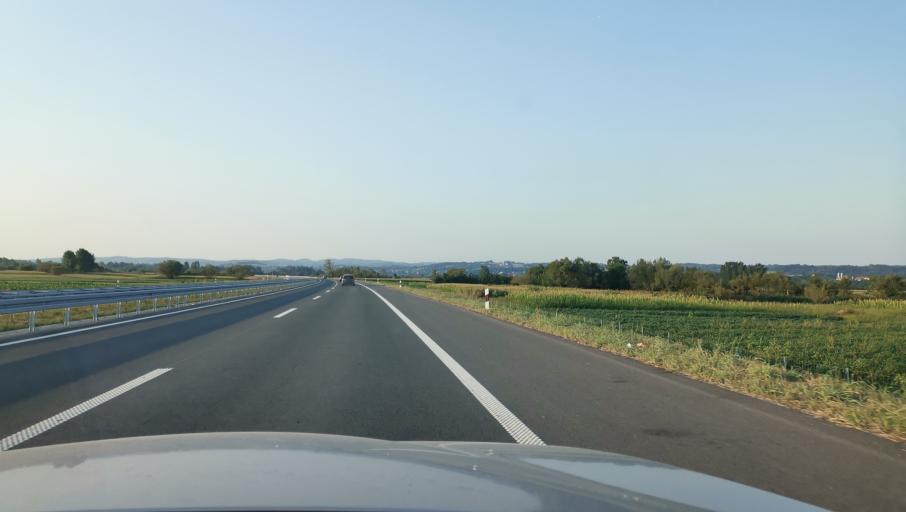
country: RS
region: Central Serbia
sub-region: Kolubarski Okrug
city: Ljig
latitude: 44.2524
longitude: 20.2698
